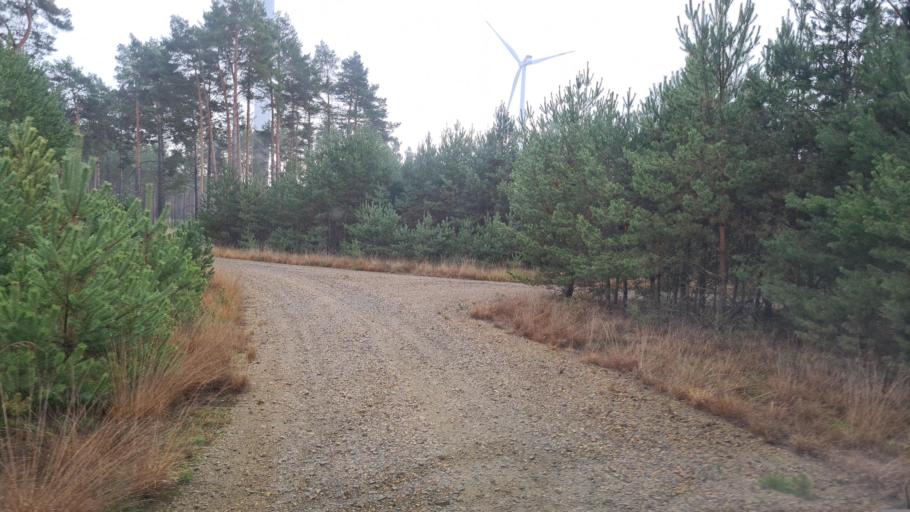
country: DE
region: Brandenburg
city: Sallgast
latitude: 51.6458
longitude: 13.8224
